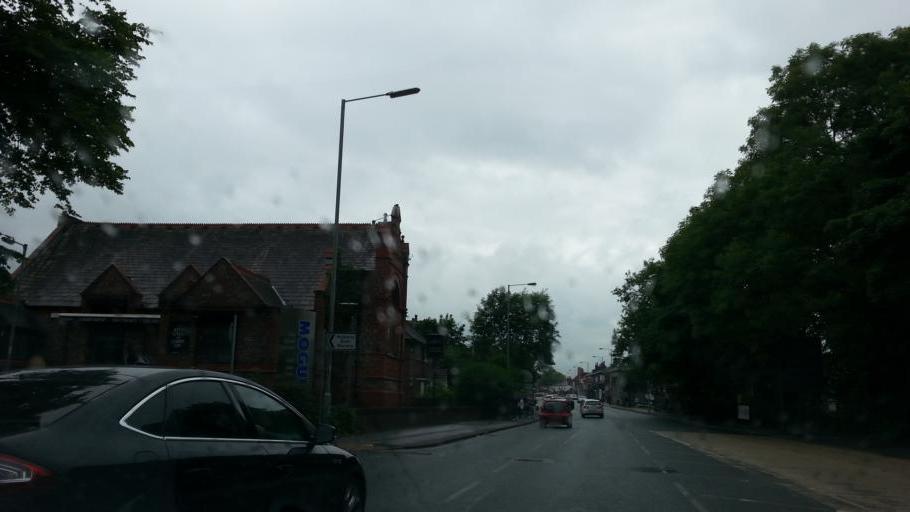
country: GB
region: England
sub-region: Borough of Bury
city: Whitefield
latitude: 53.5450
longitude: -2.2914
